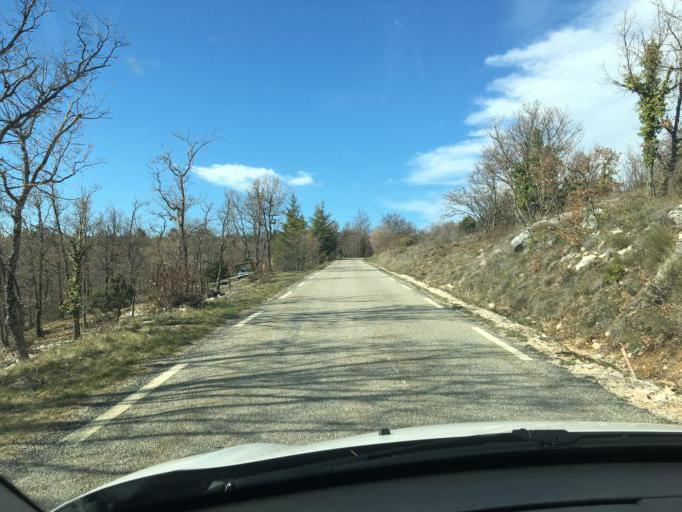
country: FR
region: Provence-Alpes-Cote d'Azur
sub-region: Departement du Vaucluse
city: Saint-Saturnin-les-Apt
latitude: 43.9712
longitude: 5.4618
